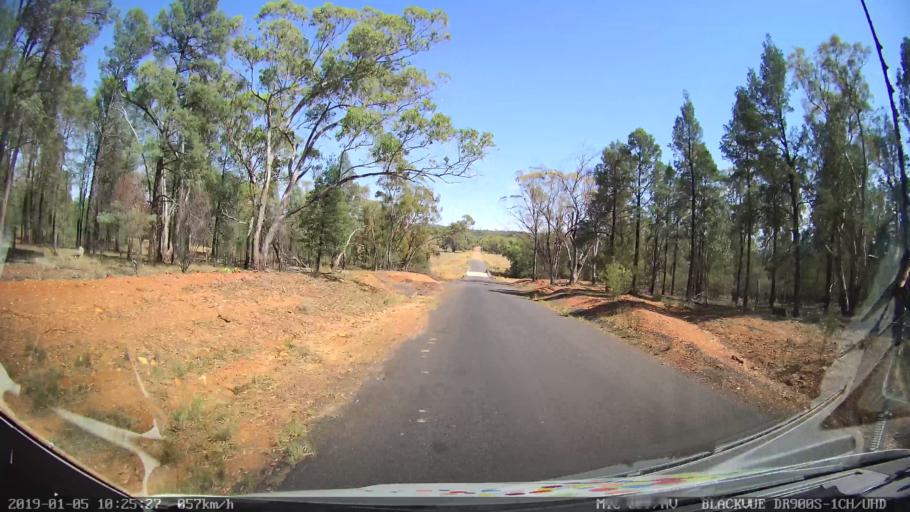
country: AU
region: New South Wales
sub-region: Gilgandra
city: Gilgandra
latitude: -31.5614
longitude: 148.9595
